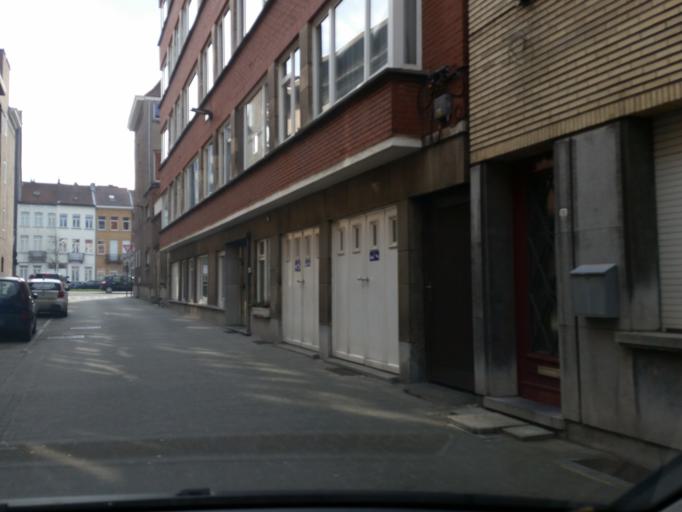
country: BE
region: Flanders
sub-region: Provincie Antwerpen
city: Mechelen
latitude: 51.0230
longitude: 4.4735
